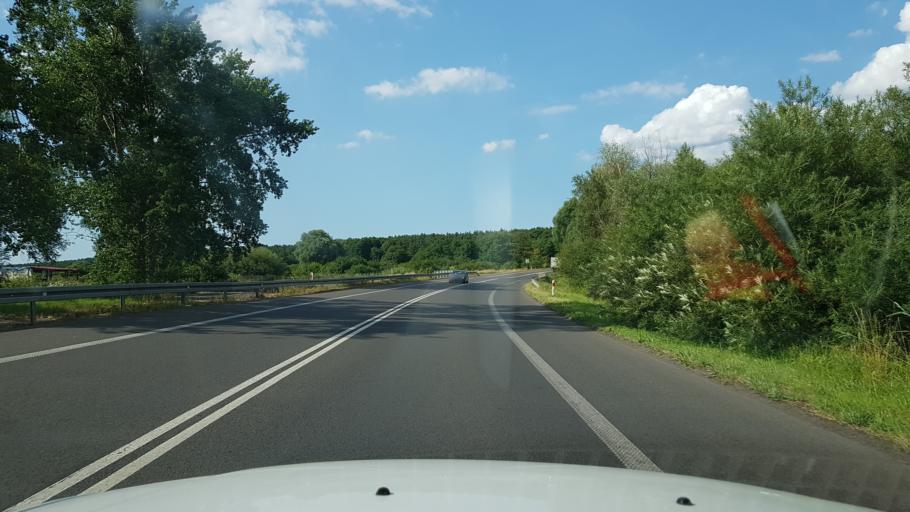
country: PL
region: West Pomeranian Voivodeship
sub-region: Powiat gryfinski
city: Stare Czarnowo
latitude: 53.2476
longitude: 14.7805
